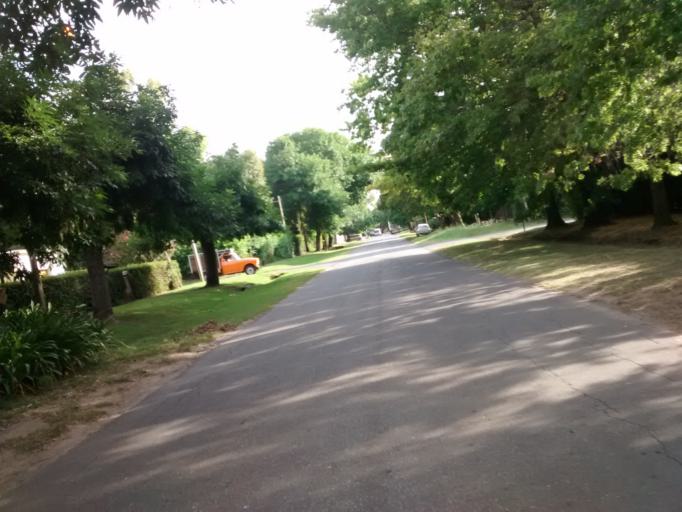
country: AR
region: Buenos Aires
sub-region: Partido de La Plata
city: La Plata
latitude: -34.8483
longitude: -58.0862
